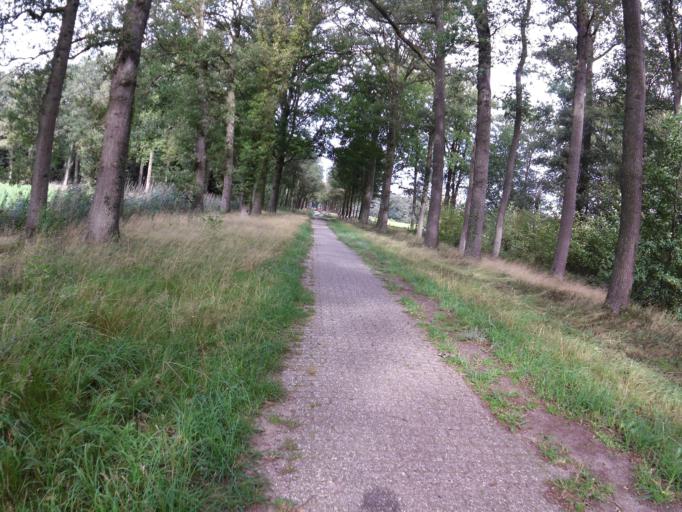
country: NL
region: Gelderland
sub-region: Gemeente Bronckhorst
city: Zelhem
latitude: 51.9592
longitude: 6.3693
